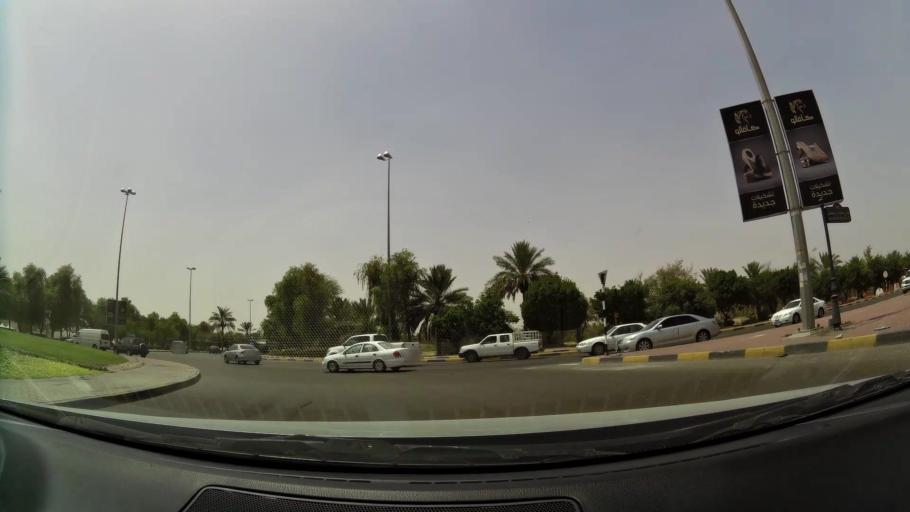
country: AE
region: Abu Dhabi
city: Al Ain
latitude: 24.1913
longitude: 55.6968
